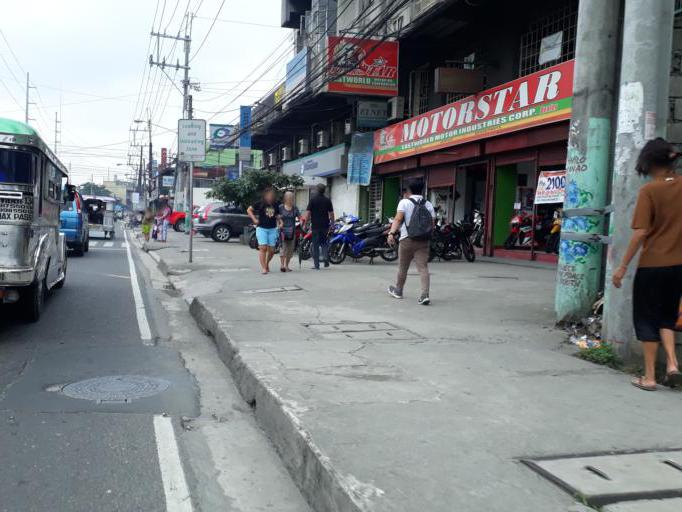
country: PH
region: Calabarzon
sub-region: Province of Rizal
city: Valenzuela
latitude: 14.6975
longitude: 120.9636
